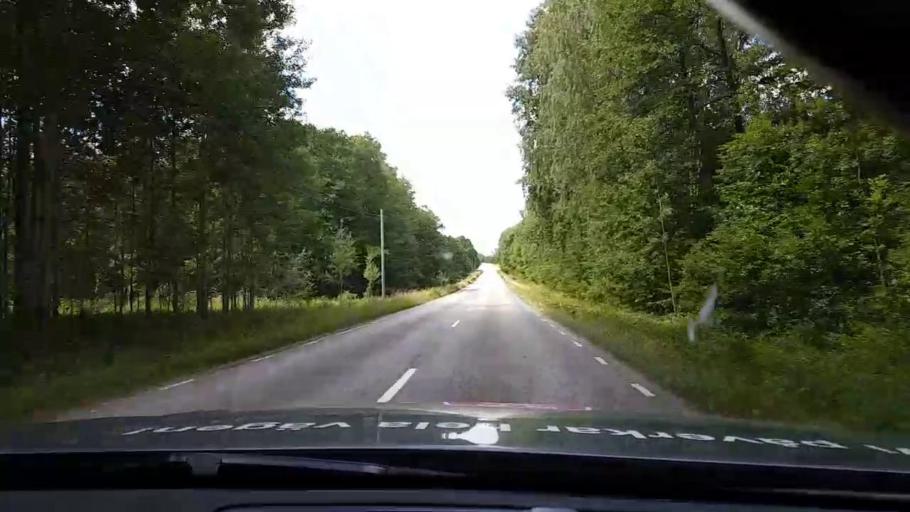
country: SE
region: Kalmar
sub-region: Vasterviks Kommun
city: Forserum
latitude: 58.0391
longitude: 16.4363
